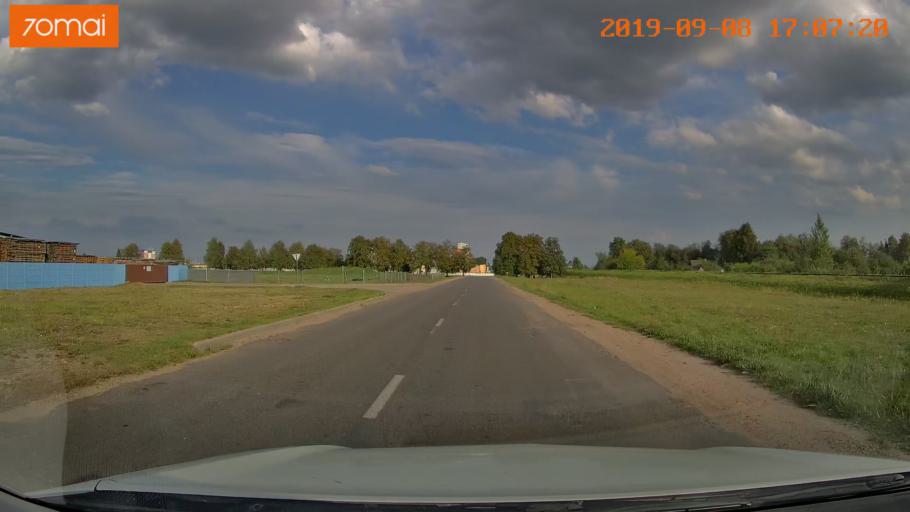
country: BY
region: Grodnenskaya
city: Hrodna
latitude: 53.6653
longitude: 23.9605
